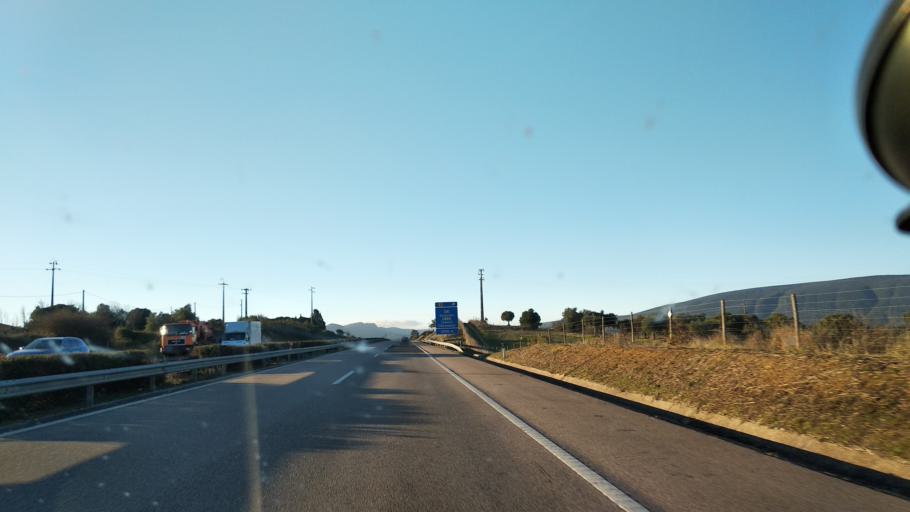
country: PT
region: Santarem
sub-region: Torres Novas
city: Torres Novas
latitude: 39.4731
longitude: -8.5972
